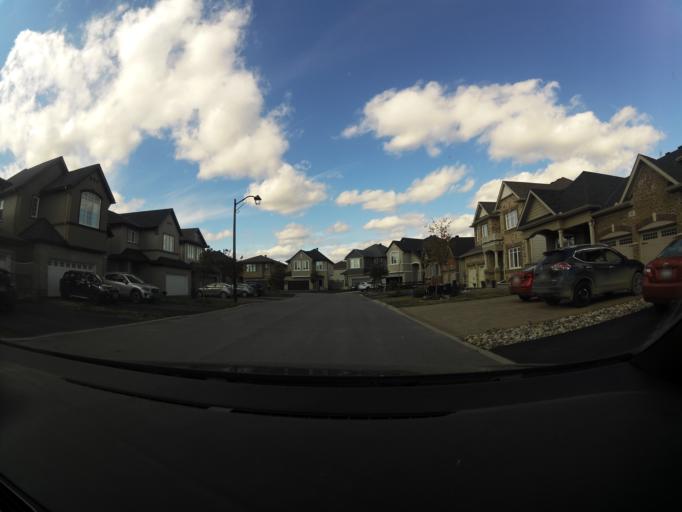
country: CA
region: Ontario
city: Bells Corners
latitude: 45.2737
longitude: -75.8865
